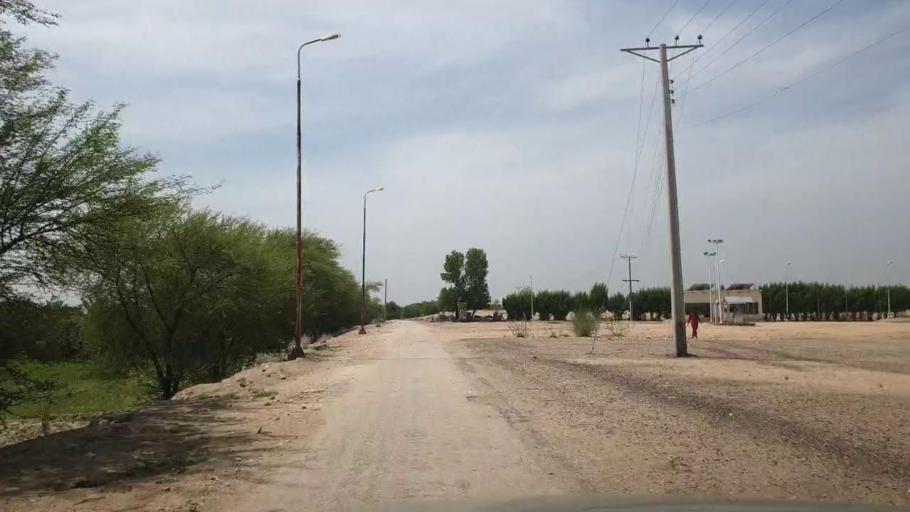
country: PK
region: Sindh
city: Kot Diji
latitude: 27.0899
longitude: 69.0749
